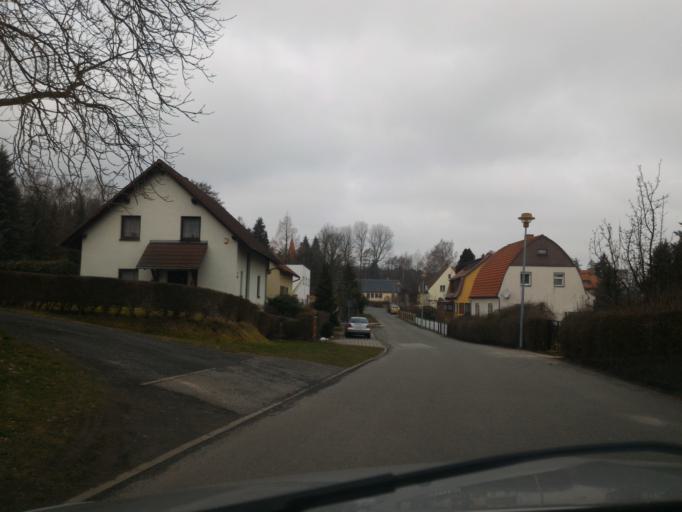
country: DE
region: Saxony
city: Olbersdorf
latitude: 50.8587
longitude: 14.7930
